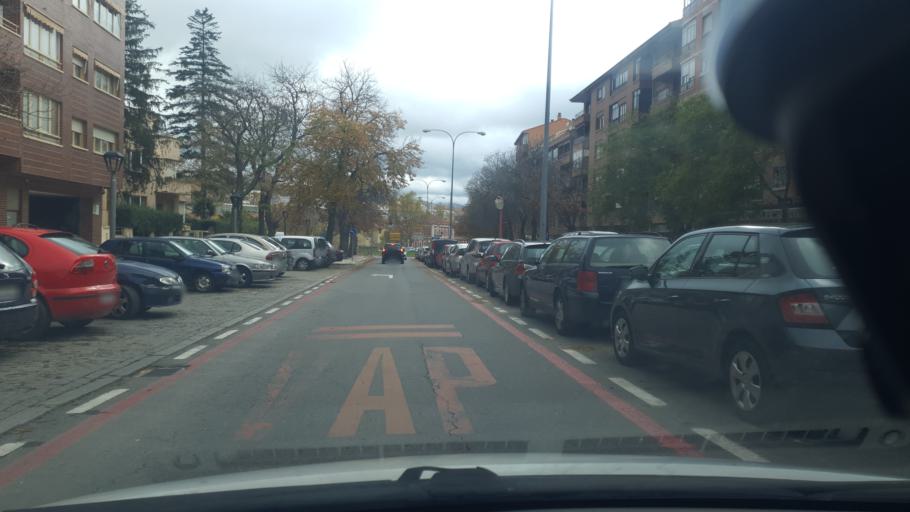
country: ES
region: Castille and Leon
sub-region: Provincia de Segovia
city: Segovia
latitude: 40.9362
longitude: -4.1136
